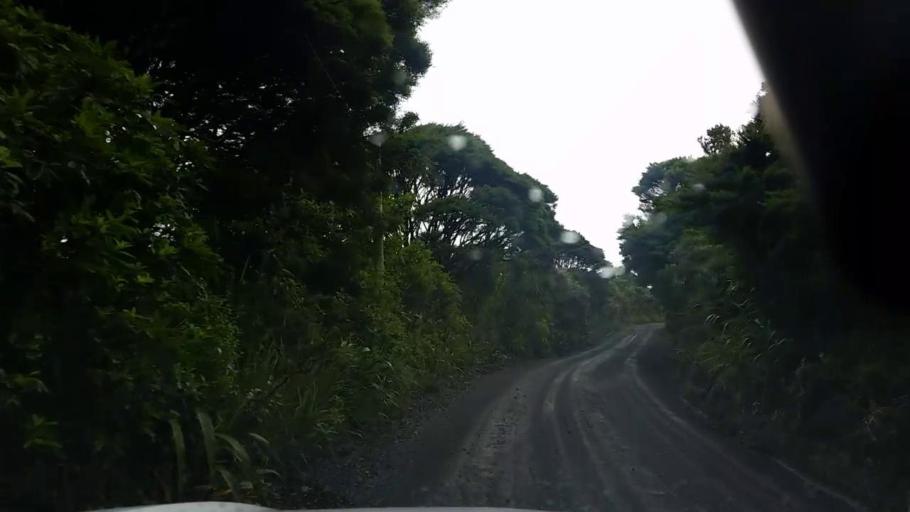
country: NZ
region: Auckland
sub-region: Auckland
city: Muriwai Beach
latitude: -36.9261
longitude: 174.4885
